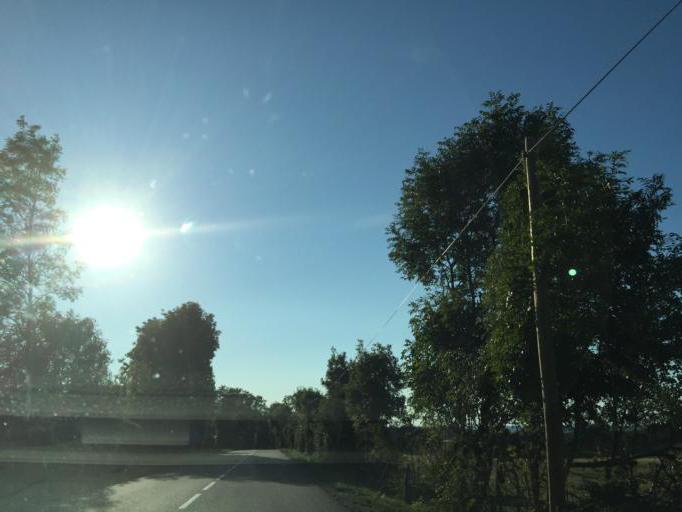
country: FR
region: Midi-Pyrenees
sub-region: Departement de l'Aveyron
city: Salles-Curan
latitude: 44.1622
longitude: 2.8038
